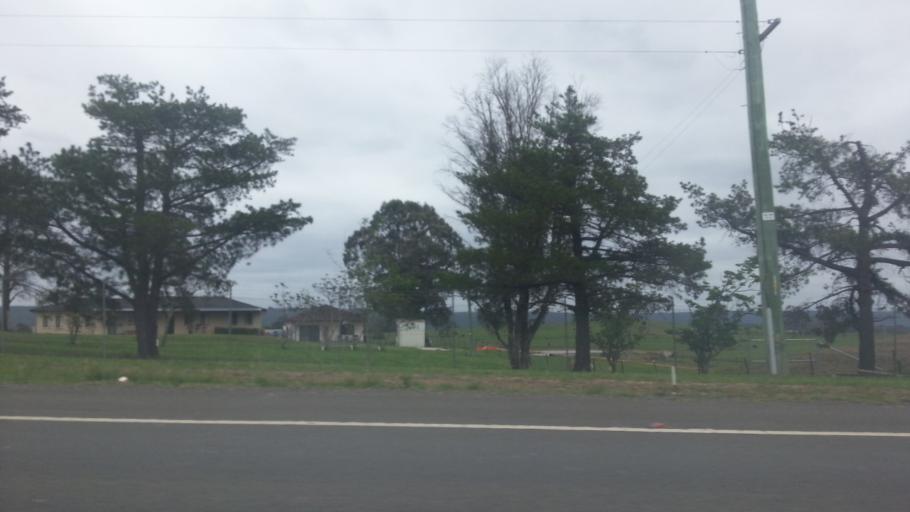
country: AU
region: New South Wales
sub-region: Penrith Municipality
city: Glenmore Park
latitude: -33.8152
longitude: 150.6895
